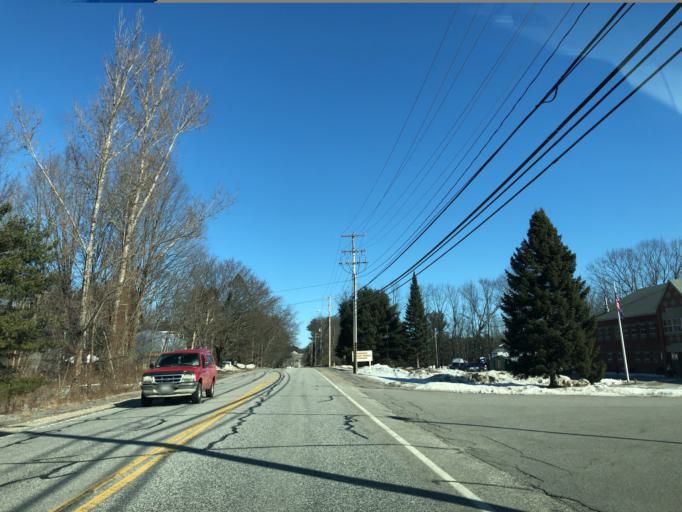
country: US
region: Maine
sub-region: Cumberland County
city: South Windham
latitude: 43.7788
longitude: -70.4161
